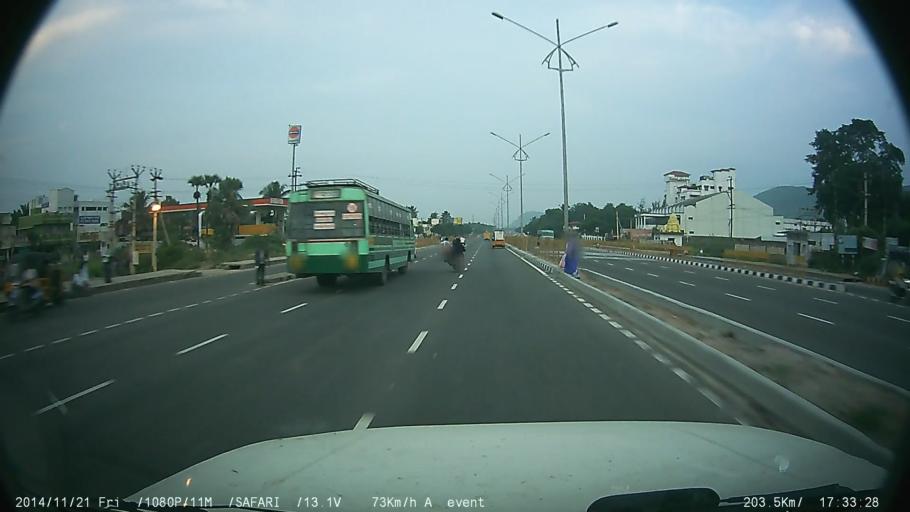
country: IN
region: Tamil Nadu
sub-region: Vellore
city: Katpadi
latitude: 12.9408
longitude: 79.1761
